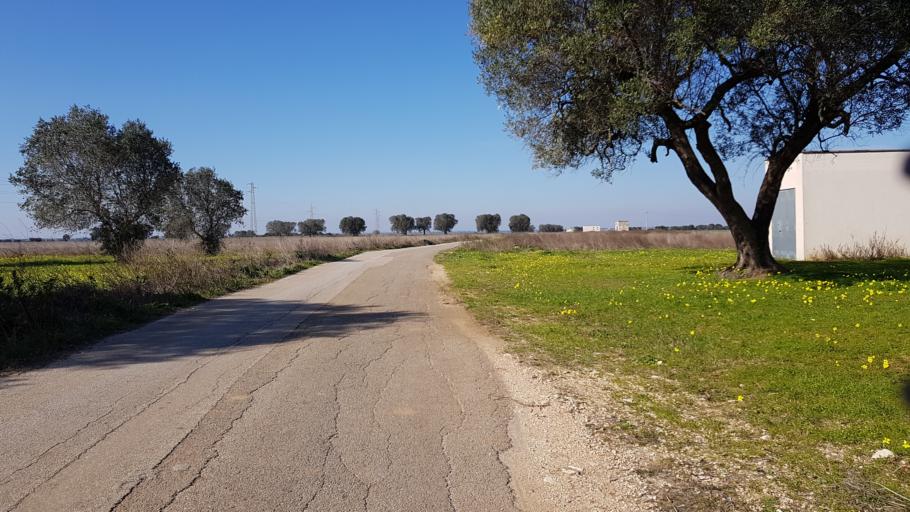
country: IT
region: Apulia
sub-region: Provincia di Brindisi
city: Mesagne
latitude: 40.6196
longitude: 17.8342
